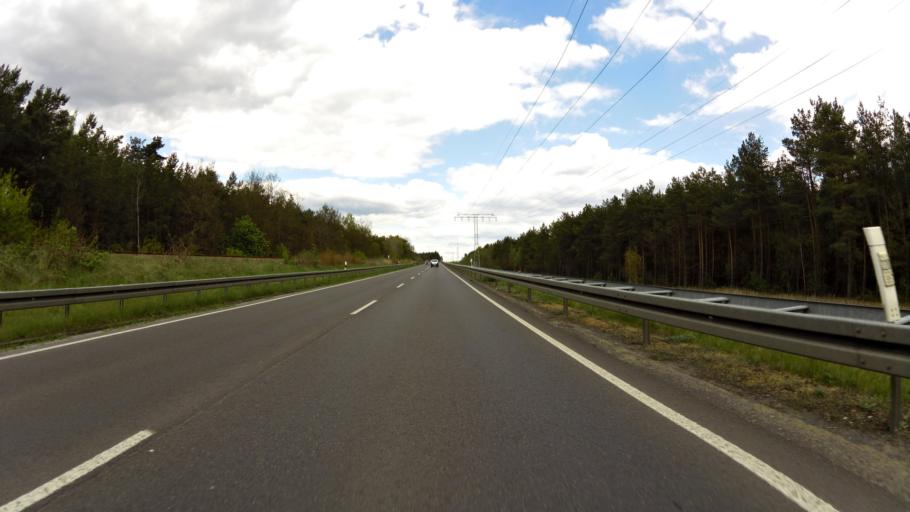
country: DE
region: Brandenburg
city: Langewahl
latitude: 52.3576
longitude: 14.1033
